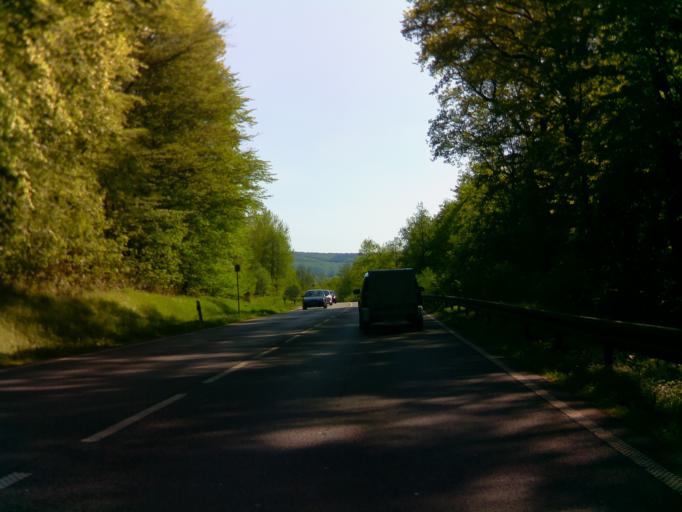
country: DE
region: Hesse
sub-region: Regierungsbezirk Darmstadt
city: Wachtersbach
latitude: 50.2435
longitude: 9.2941
